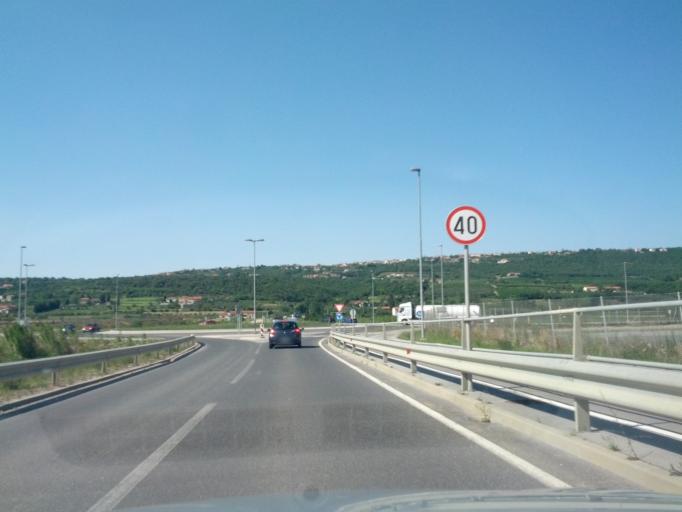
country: SI
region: Koper-Capodistria
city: Hrvatini
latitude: 45.5612
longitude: 13.7580
